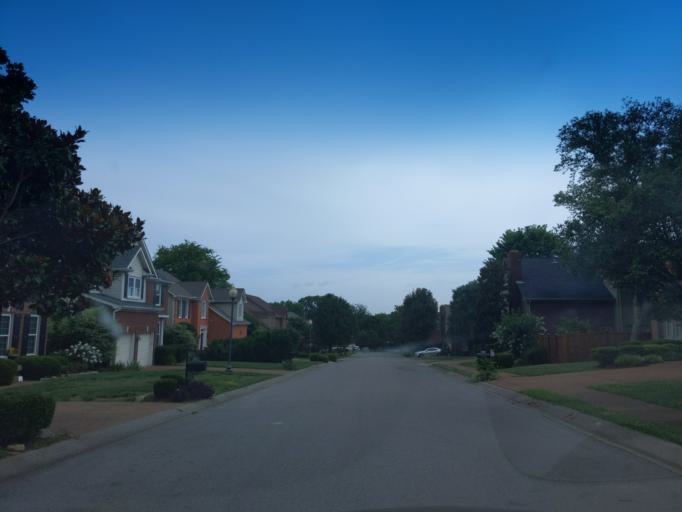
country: US
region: Tennessee
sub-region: Williamson County
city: Brentwood Estates
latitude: 36.0346
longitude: -86.7640
